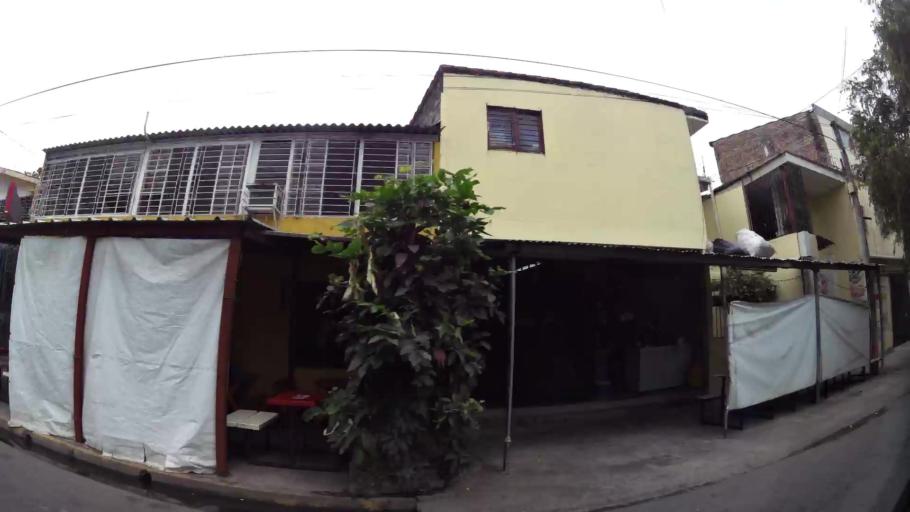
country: SV
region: San Salvador
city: San Salvador
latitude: 13.7026
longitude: -89.2187
